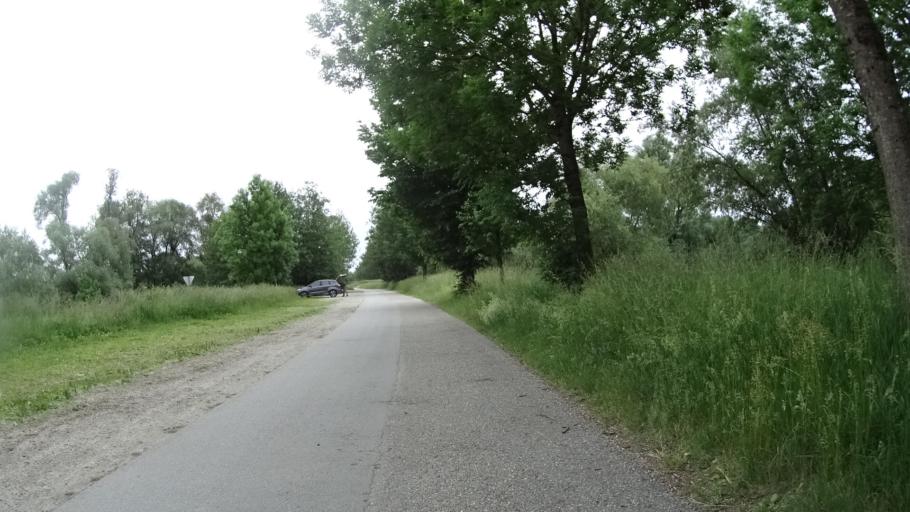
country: DE
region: Bavaria
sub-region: Lower Bavaria
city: Niederalteich
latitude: 48.7806
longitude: 13.0080
